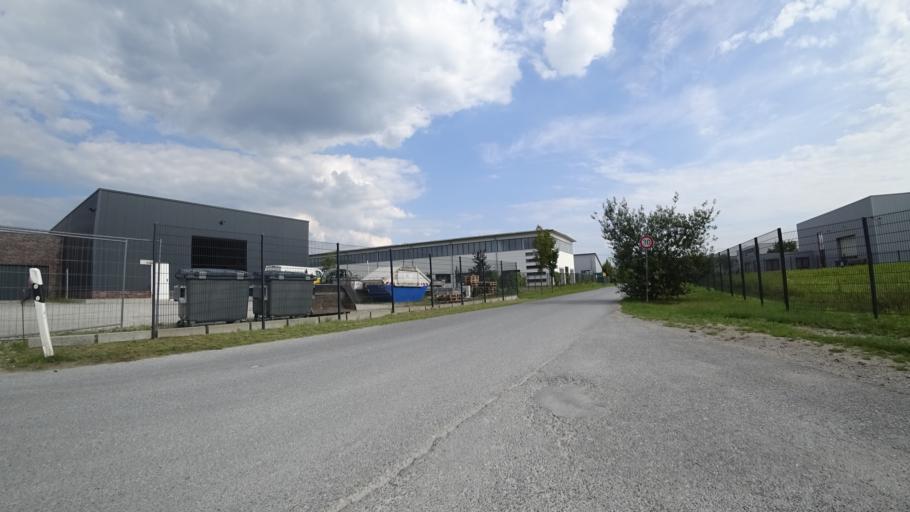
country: DE
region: North Rhine-Westphalia
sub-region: Regierungsbezirk Detmold
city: Guetersloh
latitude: 51.9318
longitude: 8.4276
